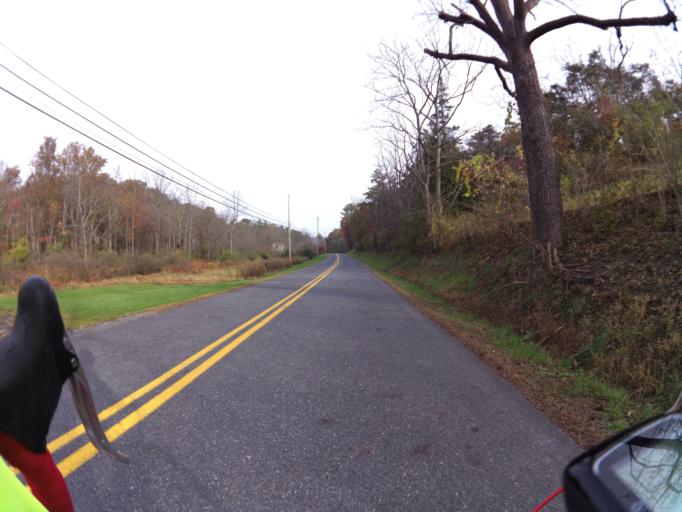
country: US
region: Pennsylvania
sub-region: Union County
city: New Columbia
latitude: 41.0334
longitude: -76.9212
